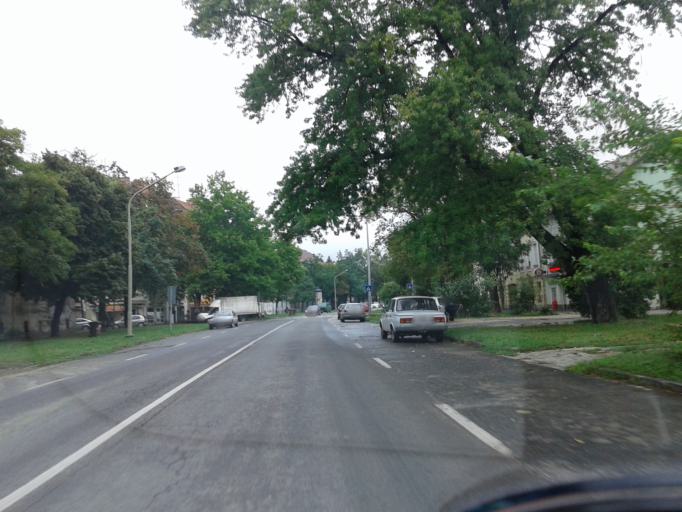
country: HU
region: Csongrad
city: Szeged
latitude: 46.2450
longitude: 20.1400
